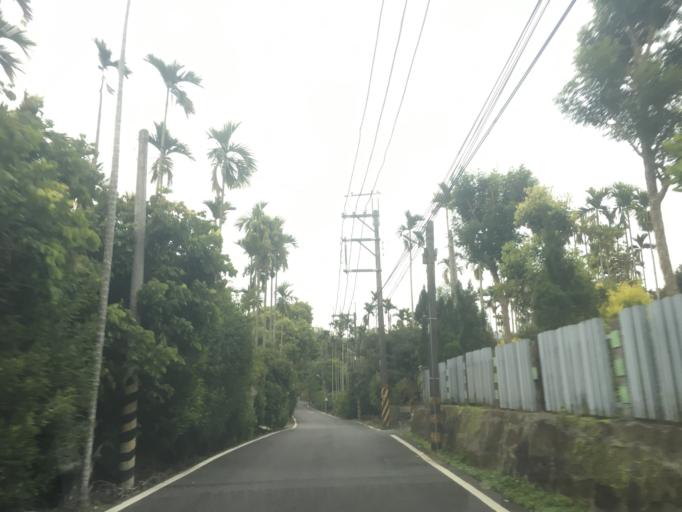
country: TW
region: Taiwan
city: Zhongxing New Village
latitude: 24.0399
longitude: 120.7161
